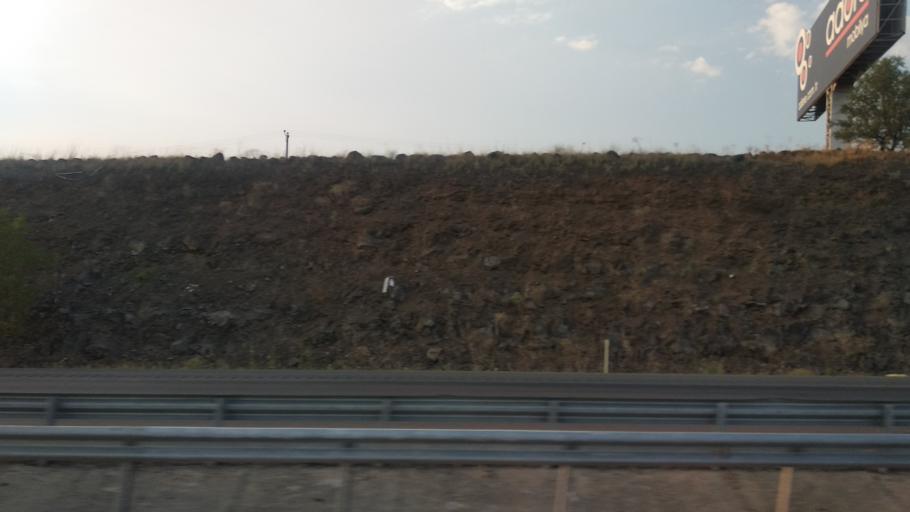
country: TR
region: Manisa
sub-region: Kula
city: Kula
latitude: 38.5595
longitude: 28.7045
